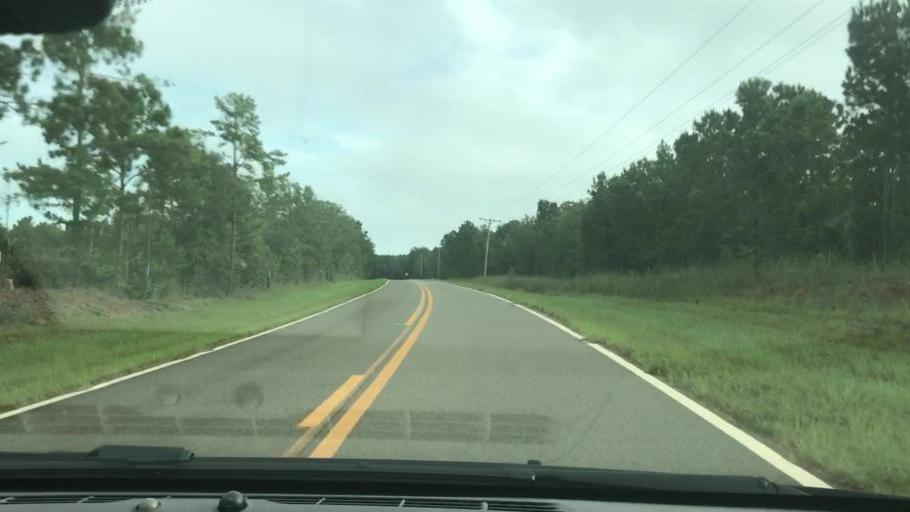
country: US
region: Georgia
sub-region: Stewart County
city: Lumpkin
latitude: 32.0382
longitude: -84.9096
